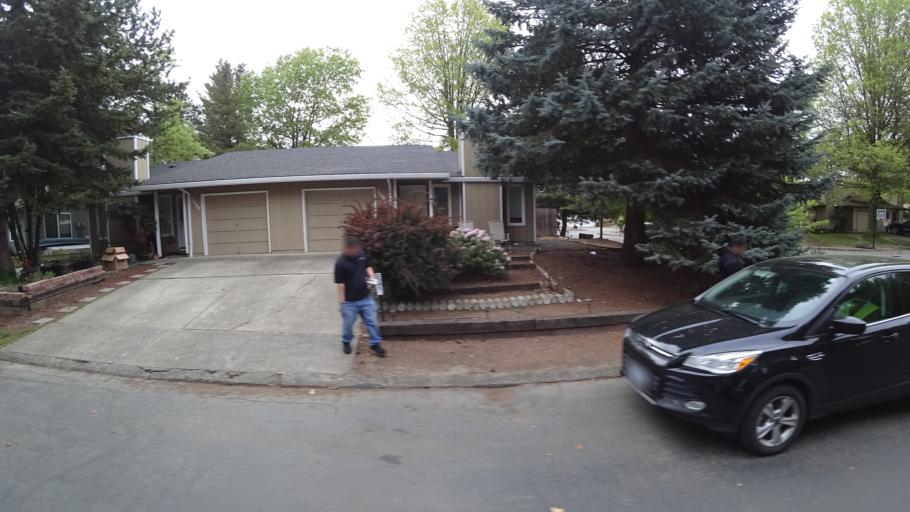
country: US
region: Oregon
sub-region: Washington County
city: Hillsboro
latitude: 45.5348
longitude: -122.9615
